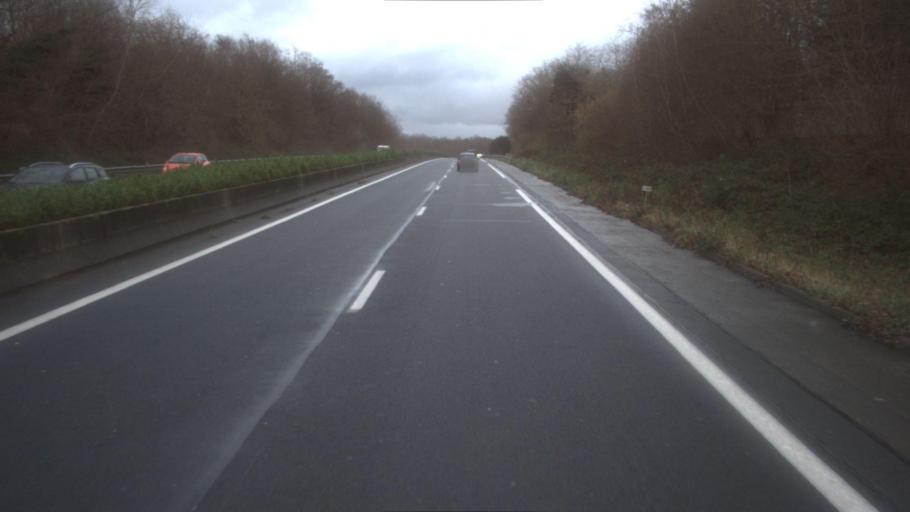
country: FR
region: Ile-de-France
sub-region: Departement de Seine-et-Marne
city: Cely
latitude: 48.4703
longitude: 2.5292
